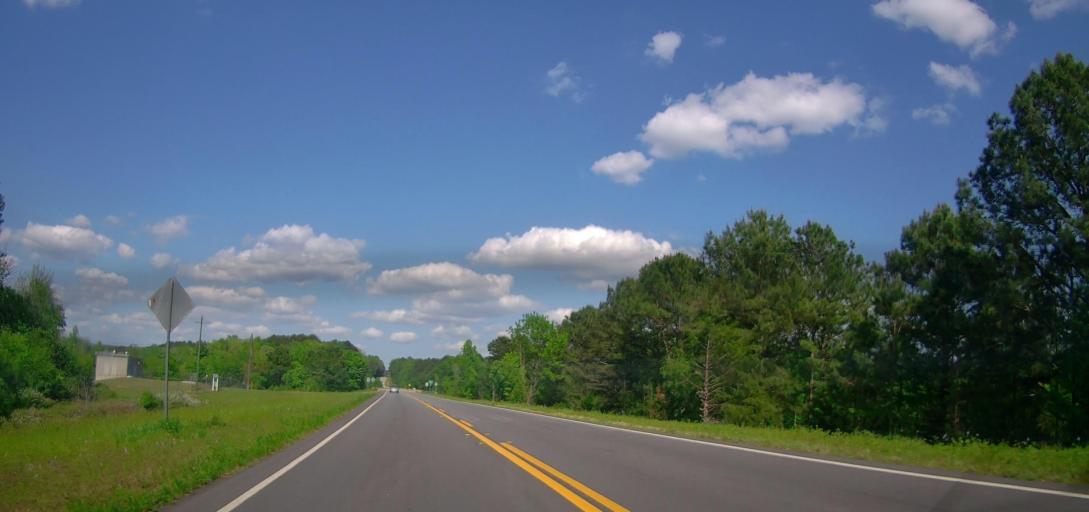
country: US
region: Georgia
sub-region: Morgan County
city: Madison
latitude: 33.6077
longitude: -83.3506
